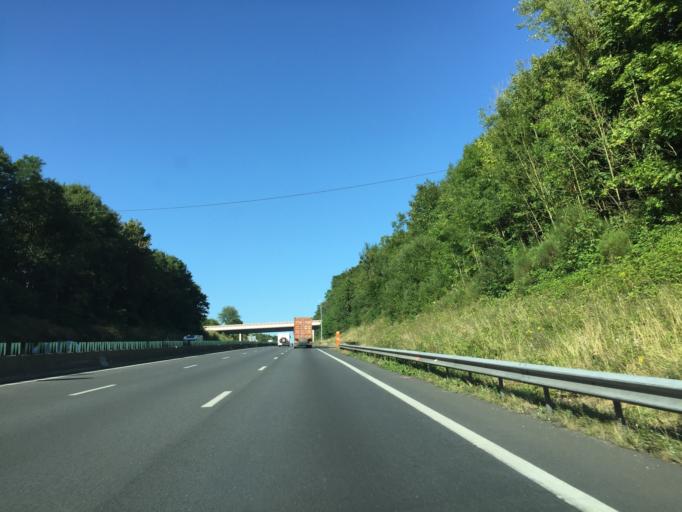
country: FR
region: Haute-Normandie
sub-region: Departement de l'Eure
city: Beuzeville
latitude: 49.3094
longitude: 0.3012
